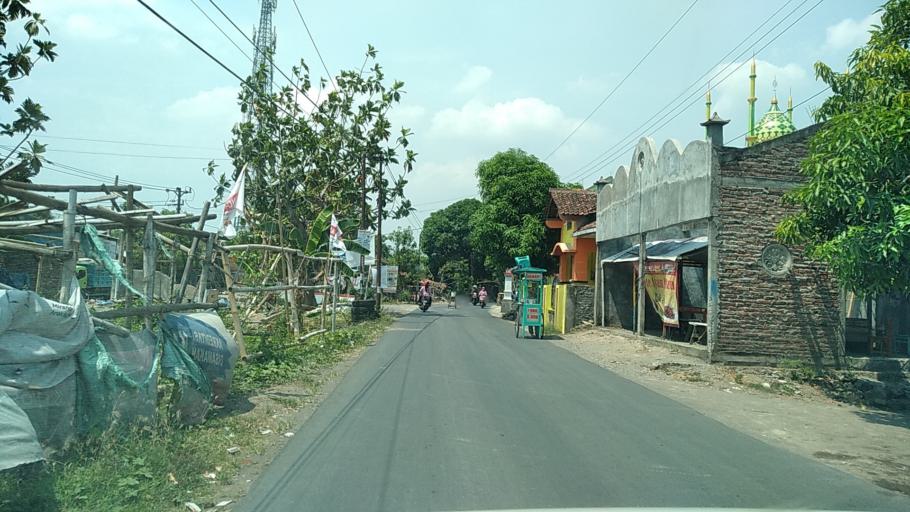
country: ID
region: Central Java
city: Mranggen
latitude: -7.0192
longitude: 110.4822
